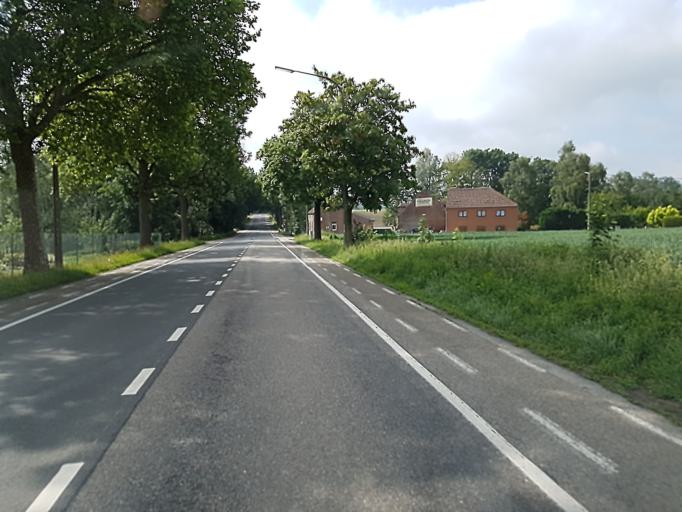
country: BE
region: Wallonia
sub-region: Province du Hainaut
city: Soignies
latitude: 50.6272
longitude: 4.0516
